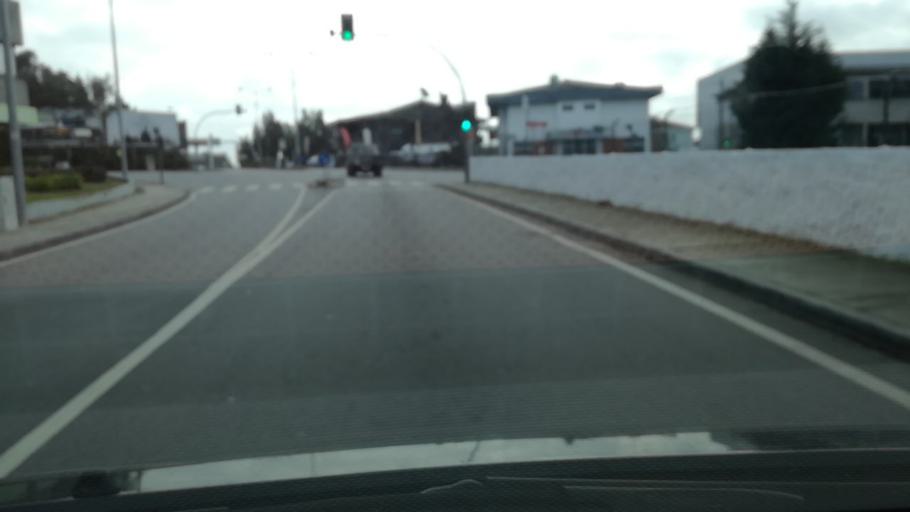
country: PT
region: Porto
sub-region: Maia
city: Gemunde
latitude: 41.2576
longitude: -8.6448
